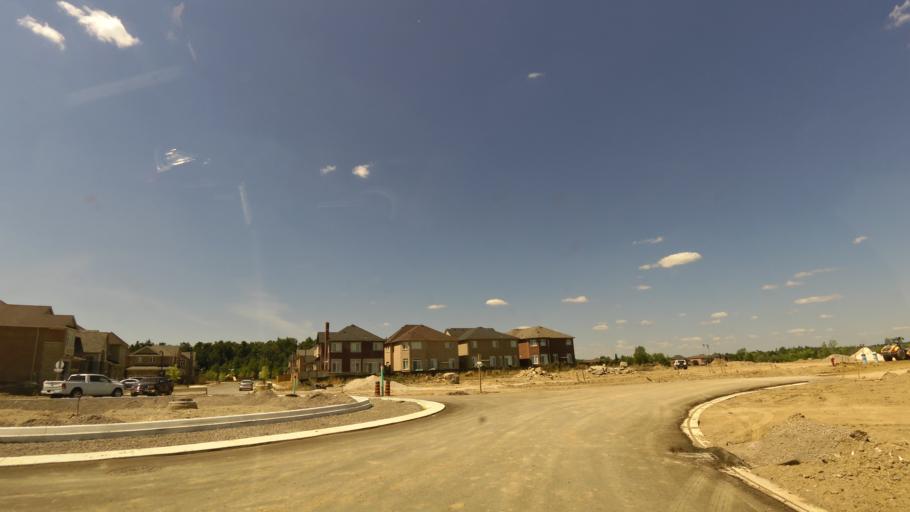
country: CA
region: Ontario
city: Brampton
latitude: 43.6348
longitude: -79.8692
